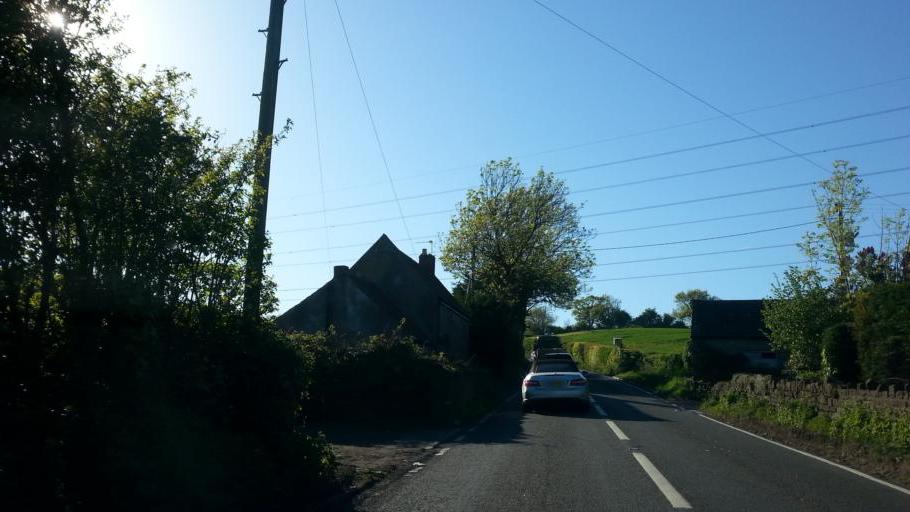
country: GB
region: England
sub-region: Somerset
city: Evercreech
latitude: 51.1640
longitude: -2.5272
